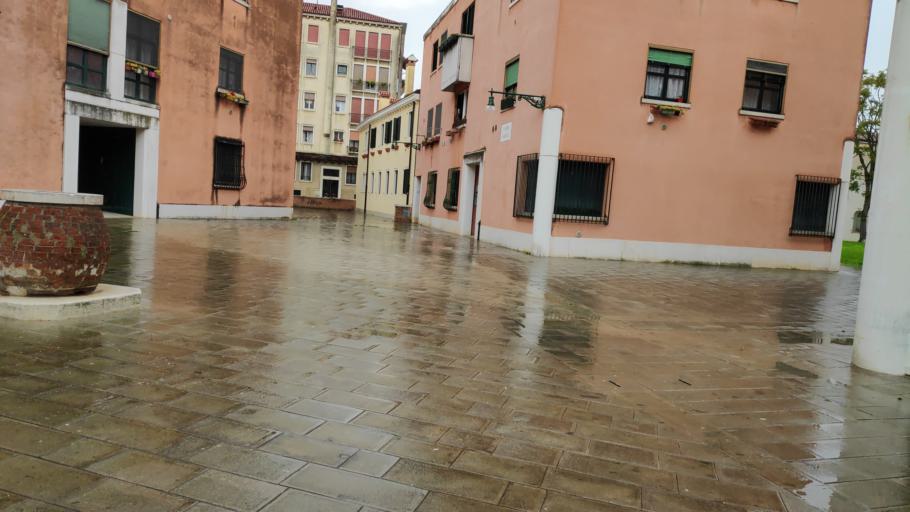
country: IT
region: Veneto
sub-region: Provincia di Venezia
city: Venice
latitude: 45.4435
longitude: 12.3214
